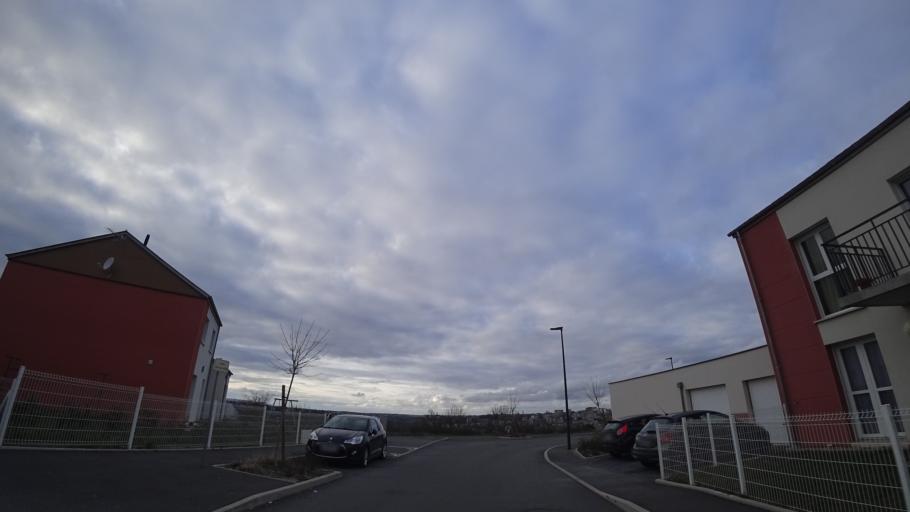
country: FR
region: Midi-Pyrenees
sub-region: Departement de l'Aveyron
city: Le Monastere
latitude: 44.3367
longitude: 2.5711
